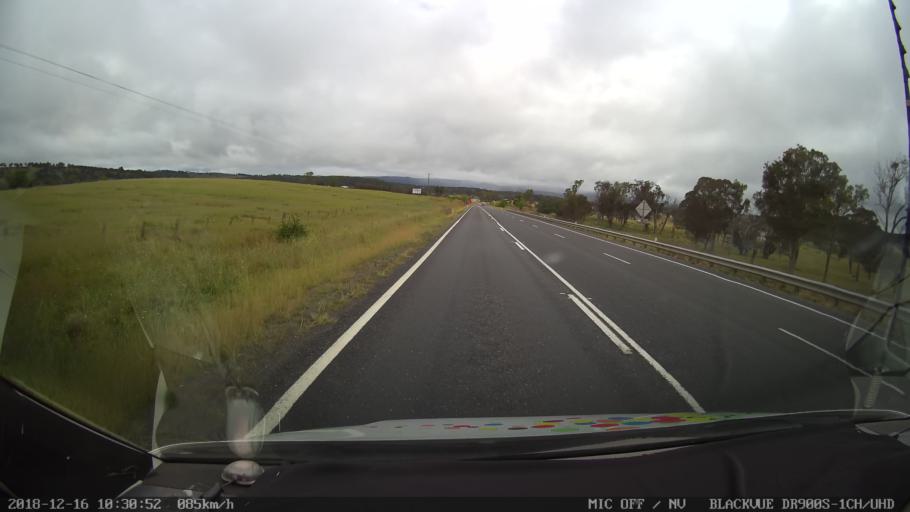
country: AU
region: New South Wales
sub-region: Tenterfield Municipality
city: Carrolls Creek
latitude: -29.0876
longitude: 152.0036
